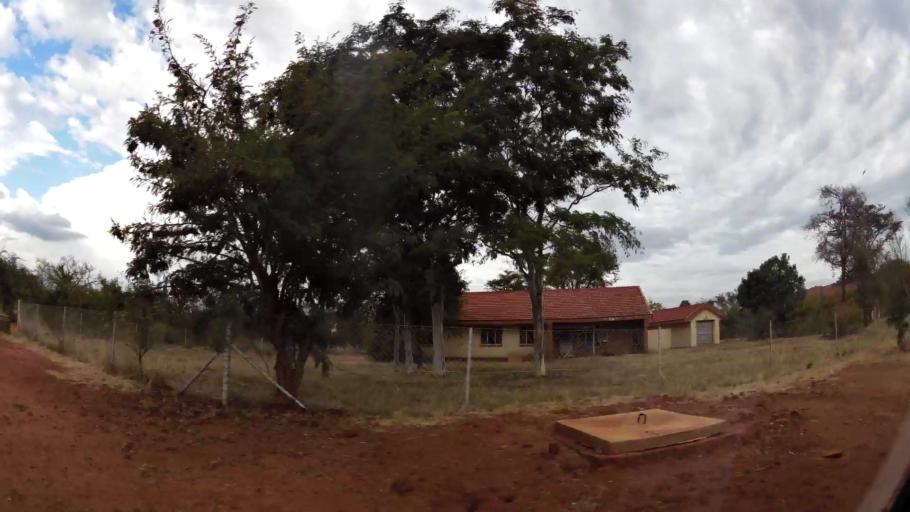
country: ZA
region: Limpopo
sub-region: Waterberg District Municipality
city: Modimolle
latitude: -24.5039
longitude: 28.7197
